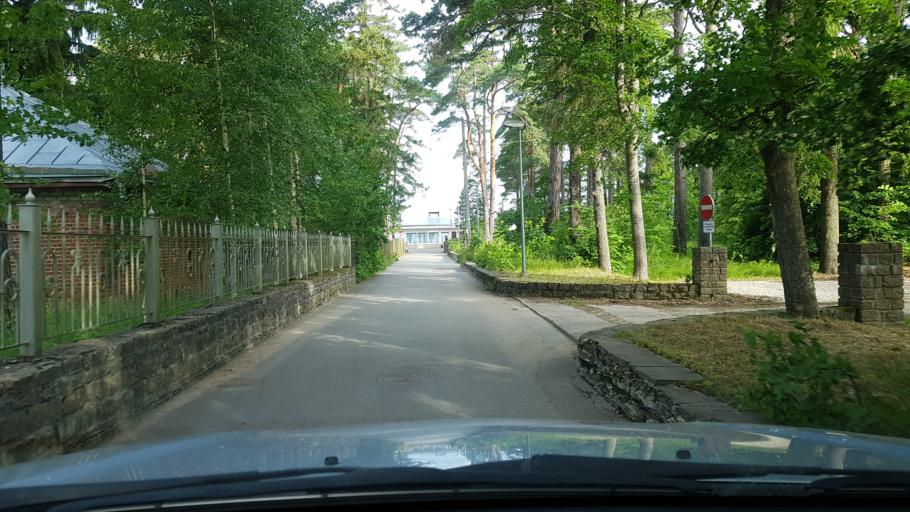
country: EE
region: Ida-Virumaa
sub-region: Narva-Joesuu linn
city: Narva-Joesuu
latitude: 59.4571
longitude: 28.0313
